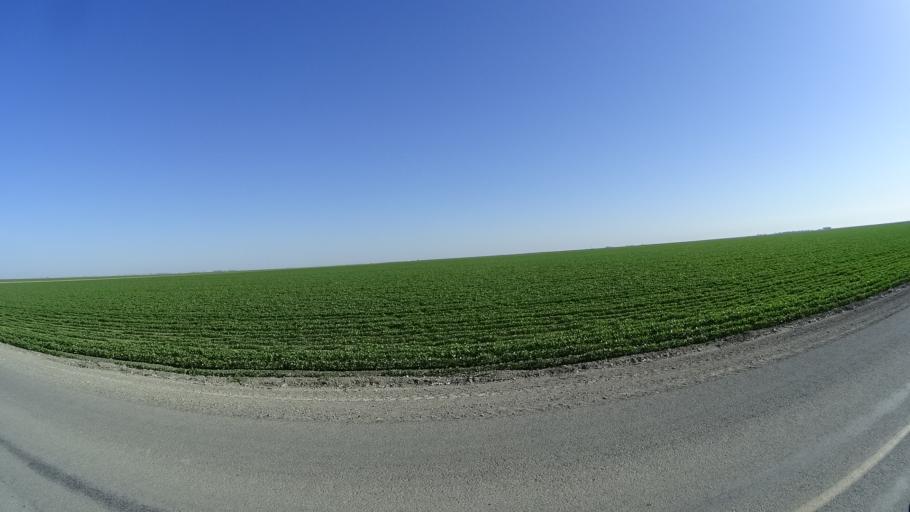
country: US
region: California
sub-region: Kings County
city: Corcoran
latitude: 36.0797
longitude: -119.6774
